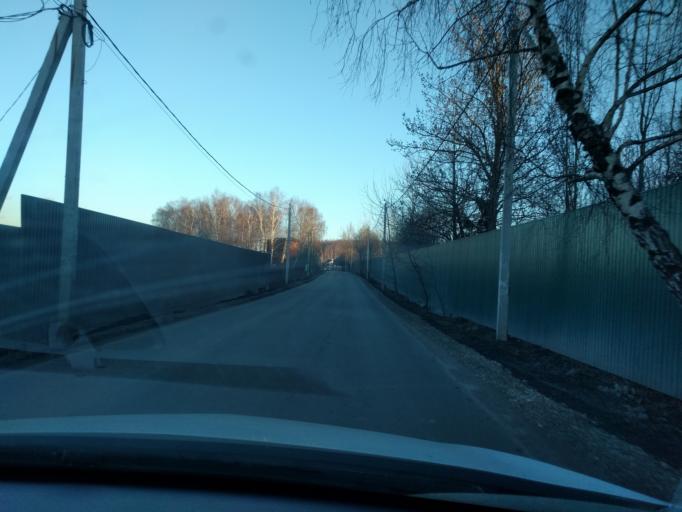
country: RU
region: Moskovskaya
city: Dubrovitsy
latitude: 55.4901
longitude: 37.4403
